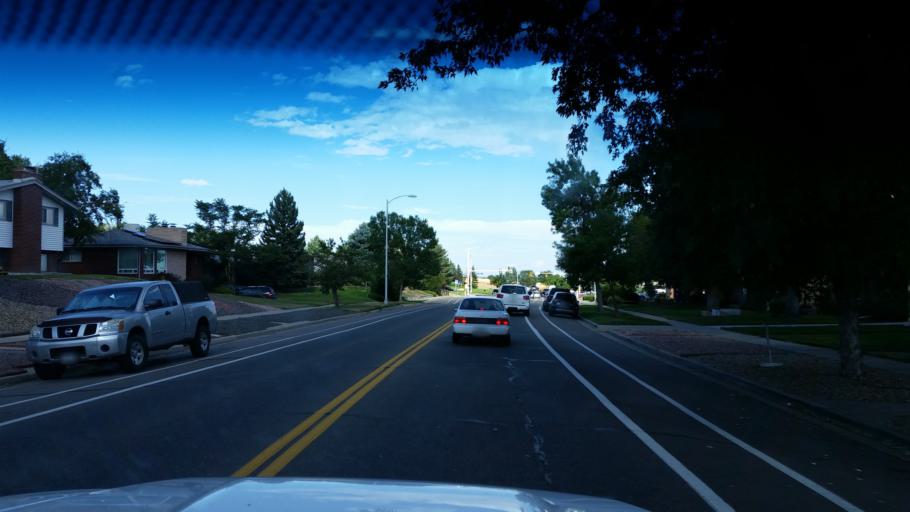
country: US
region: Colorado
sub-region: Broomfield County
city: Broomfield
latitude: 39.9249
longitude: -105.0742
